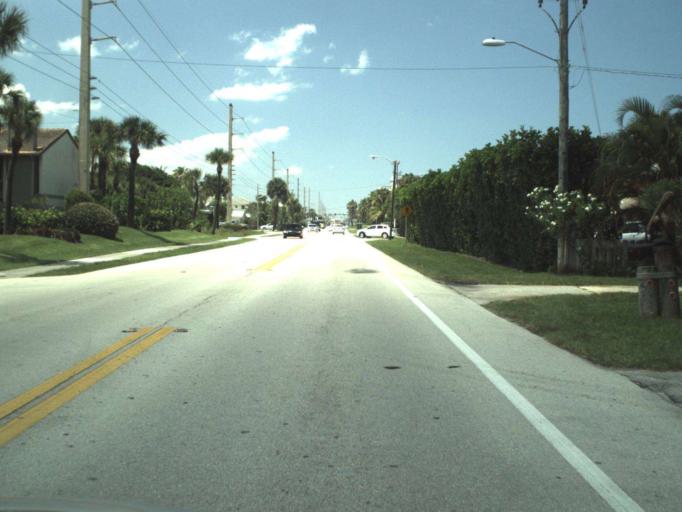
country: US
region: Florida
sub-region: Brevard County
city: Indialantic
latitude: 28.0866
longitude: -80.5650
